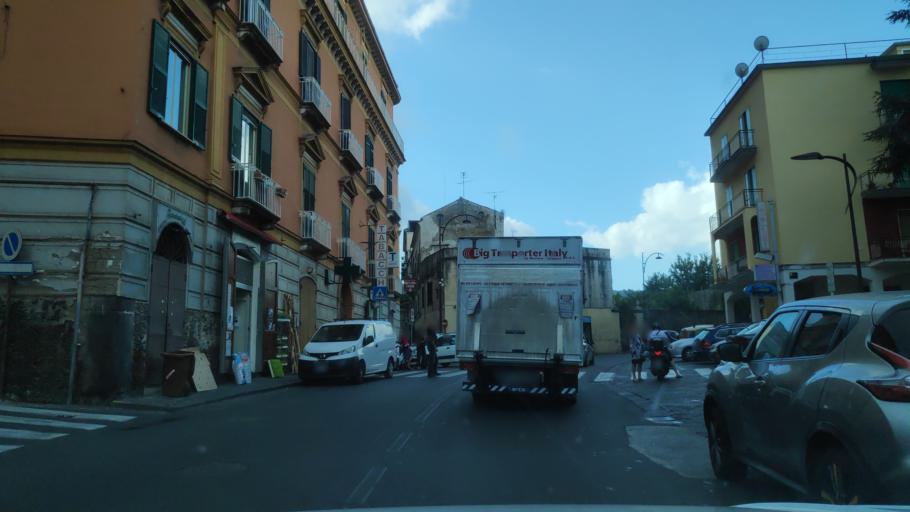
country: IT
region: Campania
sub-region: Provincia di Napoli
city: Meta
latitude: 40.6374
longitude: 14.4194
